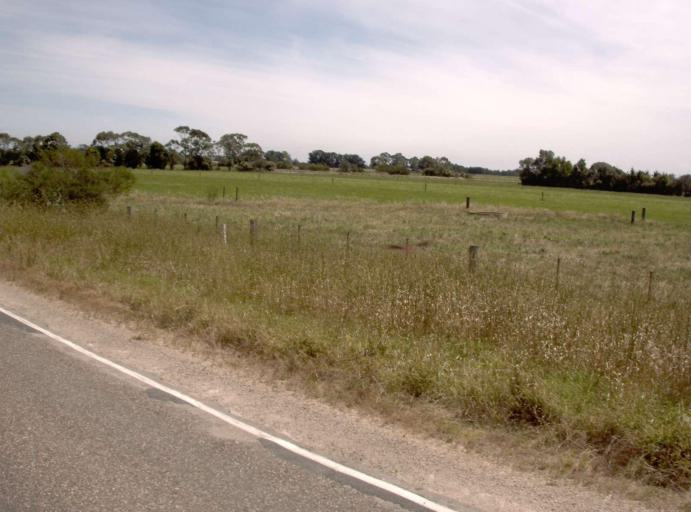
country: AU
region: Victoria
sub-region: Wellington
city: Heyfield
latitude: -38.0465
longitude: 146.8759
